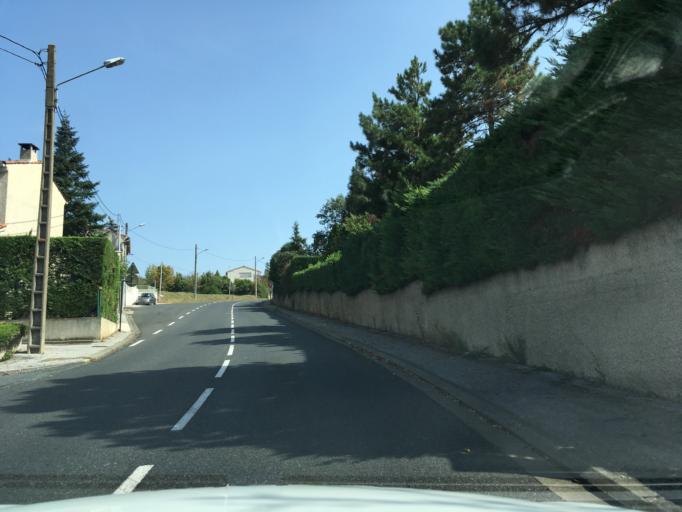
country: FR
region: Midi-Pyrenees
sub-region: Departement du Tarn
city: Castres
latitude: 43.5965
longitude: 2.2654
